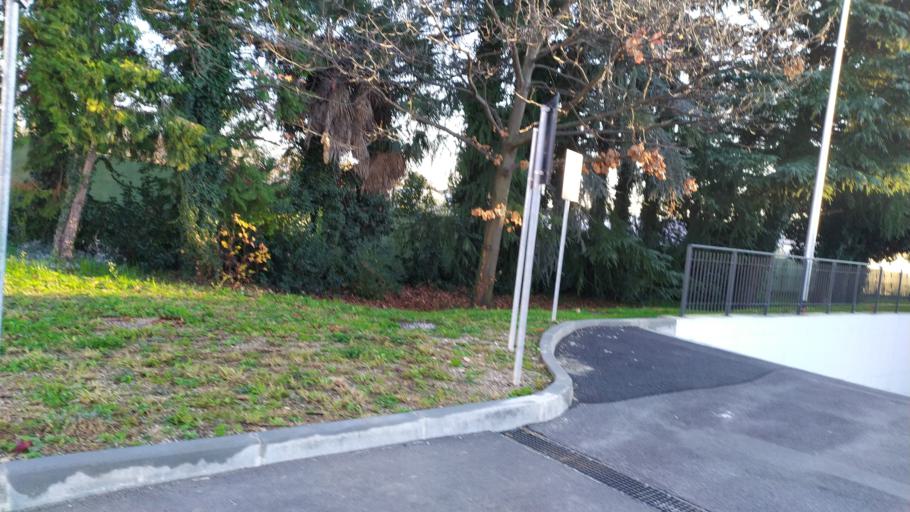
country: IT
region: Veneto
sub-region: Provincia di Vicenza
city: Schio
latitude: 45.7076
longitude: 11.3685
